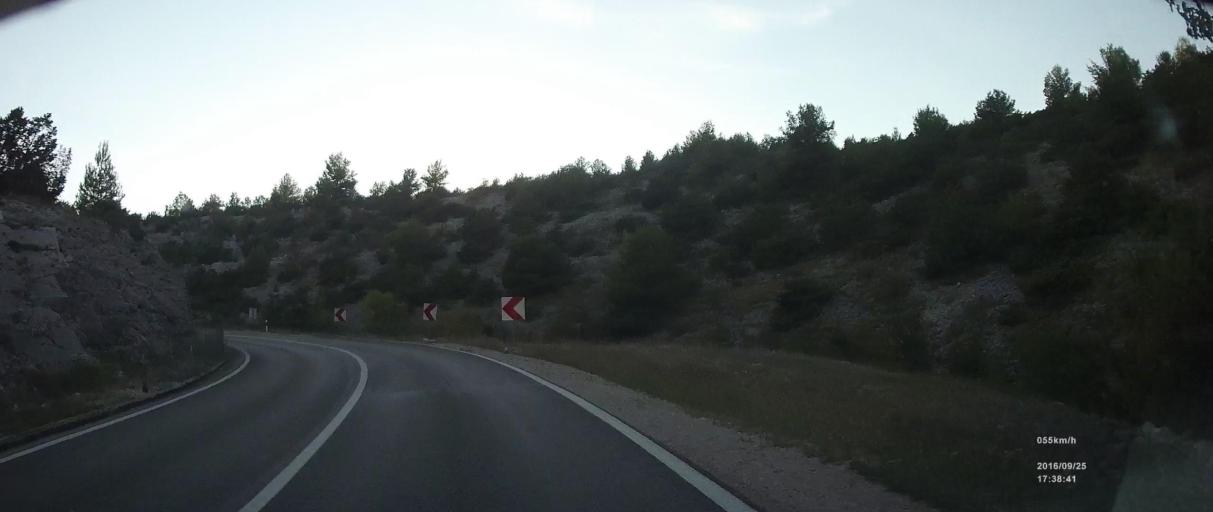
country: HR
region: Sibensko-Kniniska
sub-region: Grad Sibenik
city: Brodarica
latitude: 43.6493
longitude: 16.0580
